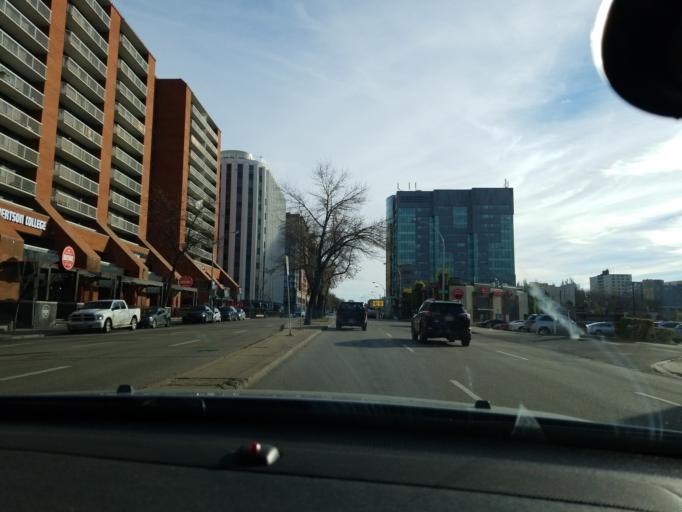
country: CA
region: Alberta
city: Edmonton
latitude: 53.5431
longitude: -113.5086
